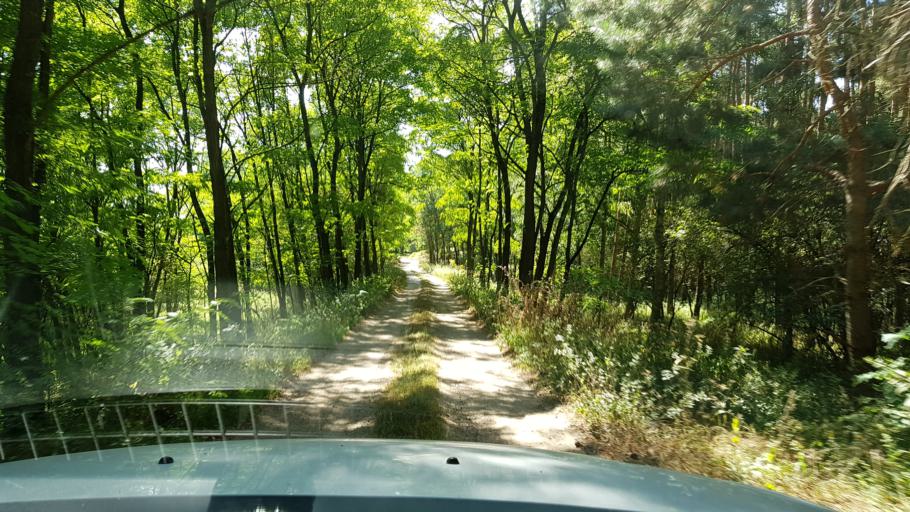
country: PL
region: West Pomeranian Voivodeship
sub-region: Powiat gryfinski
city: Cedynia
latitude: 52.8388
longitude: 14.2548
